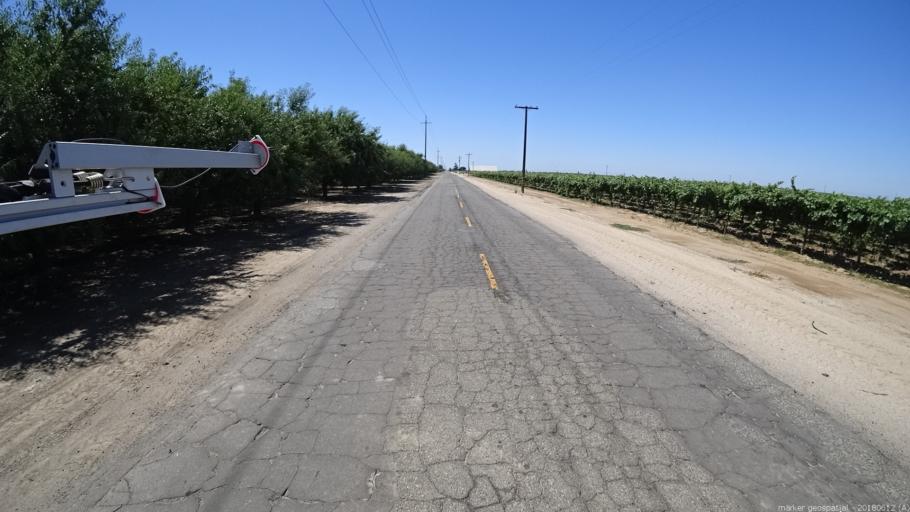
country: US
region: California
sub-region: Madera County
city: Chowchilla
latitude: 37.0274
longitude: -120.3286
